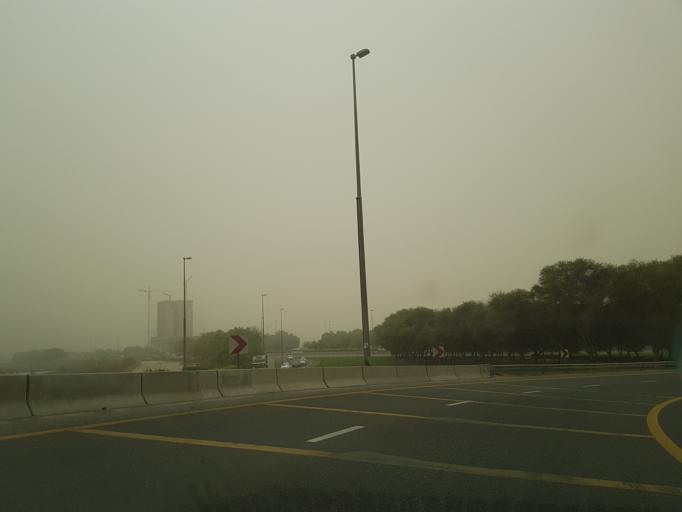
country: AE
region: Ash Shariqah
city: Sharjah
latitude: 25.1823
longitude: 55.3156
